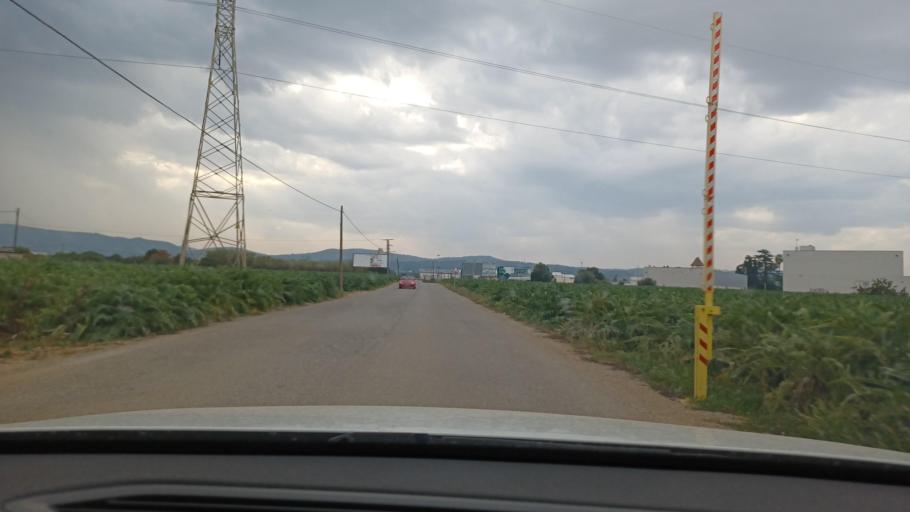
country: ES
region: Valencia
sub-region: Provincia de Castello
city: Benicarlo
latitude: 40.4080
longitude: 0.3967
